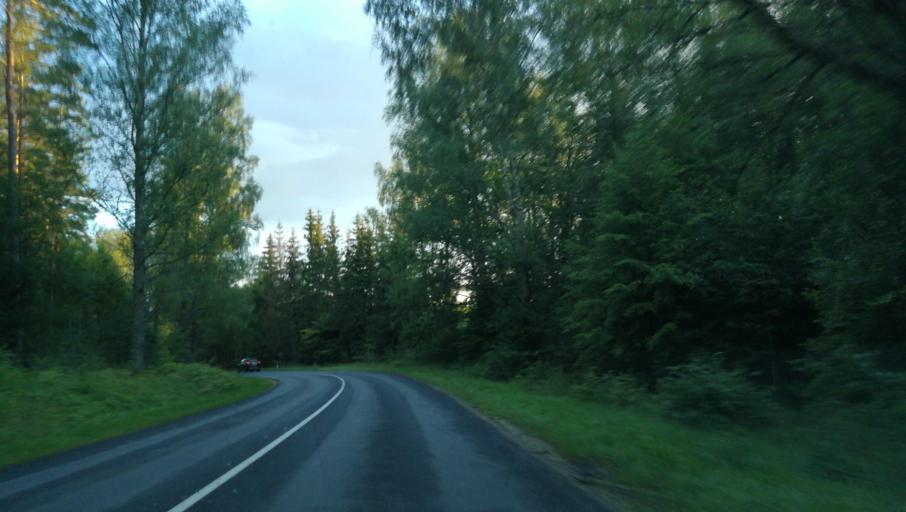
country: LV
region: Priekuli
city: Priekuli
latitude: 57.3680
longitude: 25.3822
